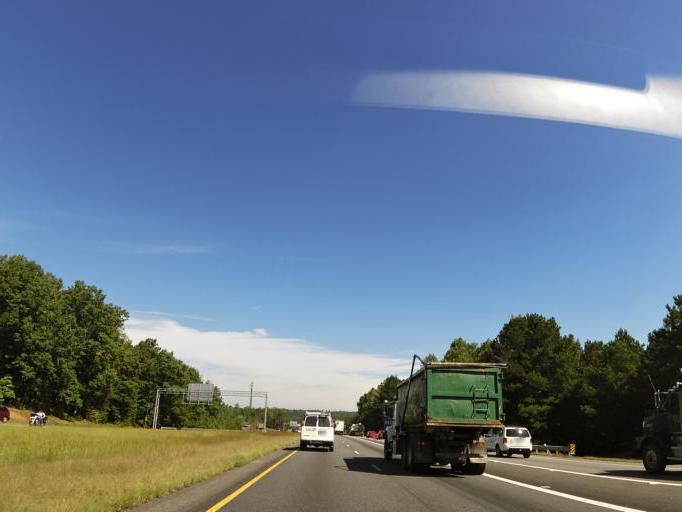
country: US
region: Georgia
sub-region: Cherokee County
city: Woodstock
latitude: 34.0895
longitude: -84.5340
